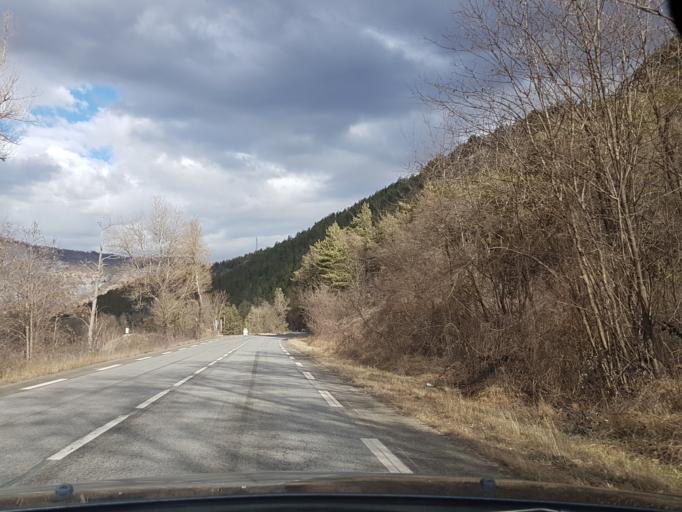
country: FR
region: Provence-Alpes-Cote d'Azur
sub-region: Departement des Hautes-Alpes
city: Tallard
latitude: 44.4957
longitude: 6.0824
